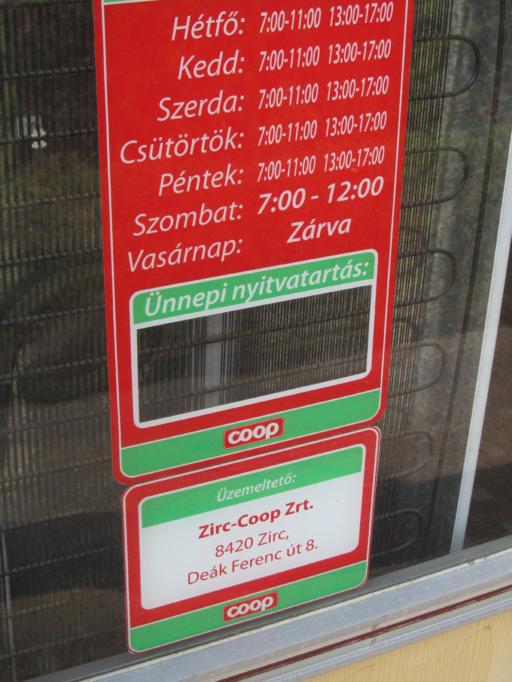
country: HU
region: Veszprem
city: Herend
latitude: 47.2557
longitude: 17.7233
